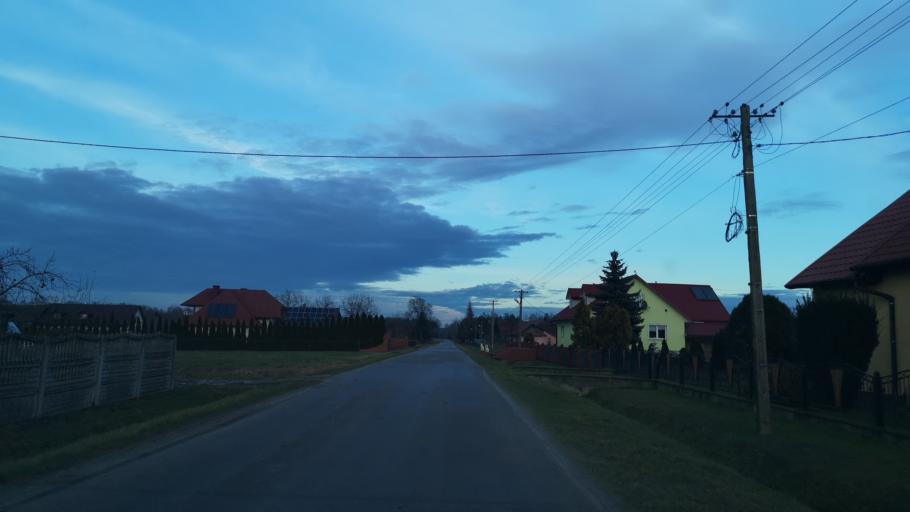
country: PL
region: Subcarpathian Voivodeship
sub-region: Powiat przeworski
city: Adamowka
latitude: 50.2525
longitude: 22.6351
